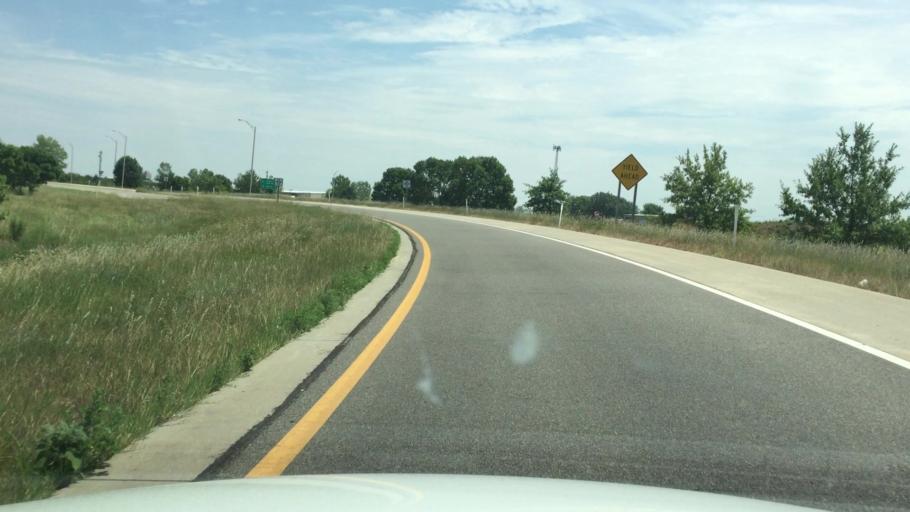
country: US
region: Kansas
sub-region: Shawnee County
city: Topeka
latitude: 39.0323
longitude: -95.6261
